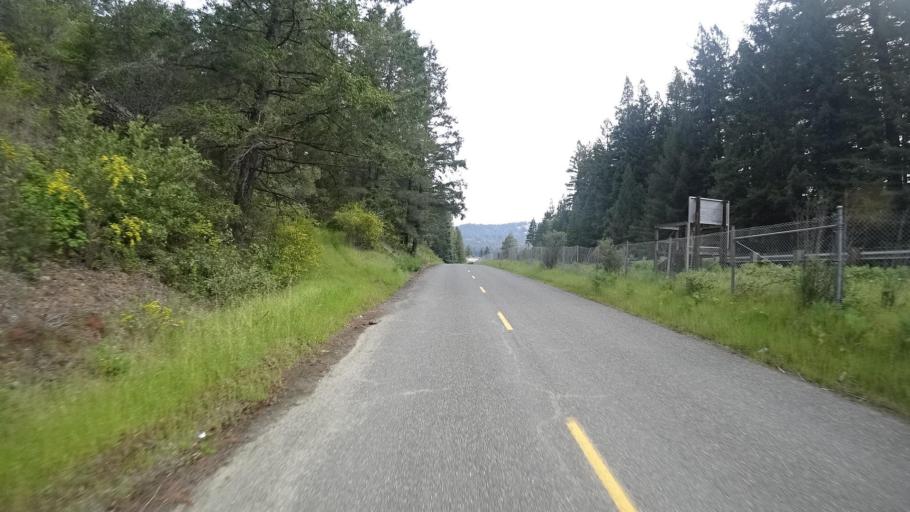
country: US
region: California
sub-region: Humboldt County
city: Redway
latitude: 40.2363
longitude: -123.8334
